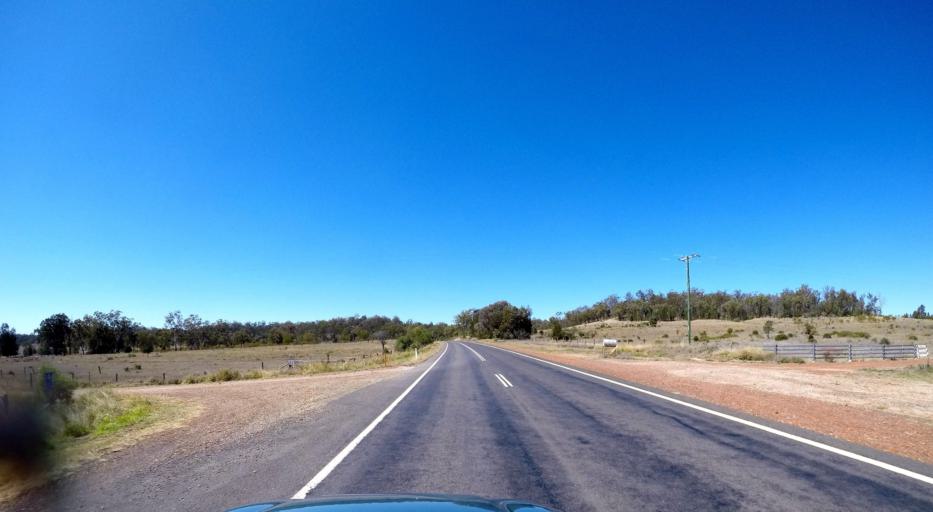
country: AU
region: Queensland
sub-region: Western Downs
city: Westcourt
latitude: -26.3584
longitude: 150.0702
